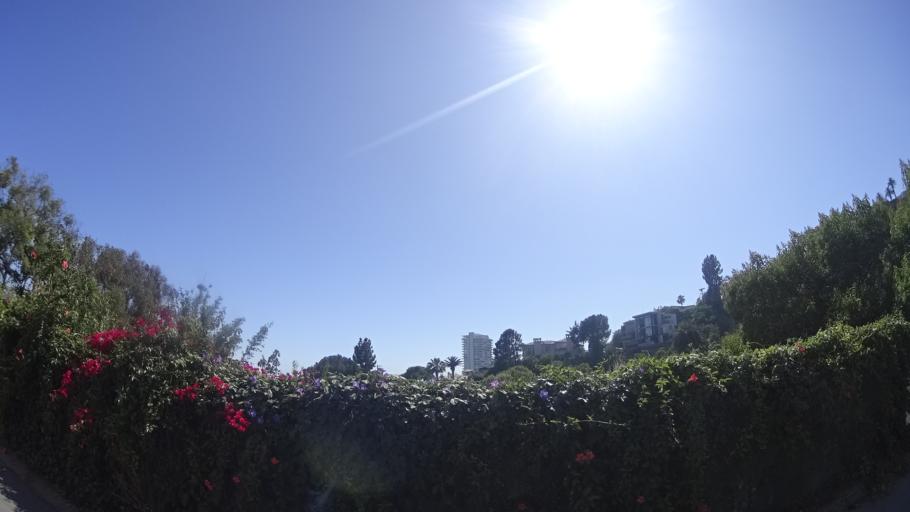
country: US
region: California
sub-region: Los Angeles County
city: Beverly Hills
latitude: 34.0936
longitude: -118.3880
